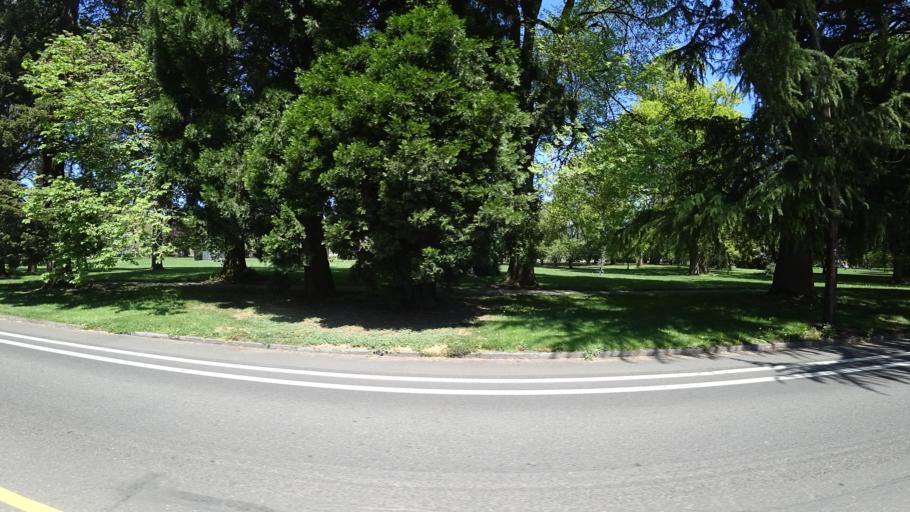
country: US
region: Oregon
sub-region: Clackamas County
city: Milwaukie
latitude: 45.4792
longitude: -122.6317
